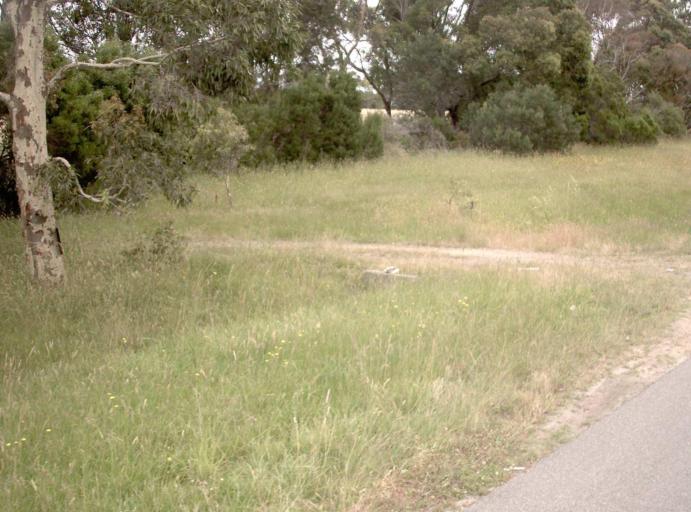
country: AU
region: Victoria
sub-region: Mornington Peninsula
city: Safety Beach
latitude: -38.3056
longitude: 145.0312
